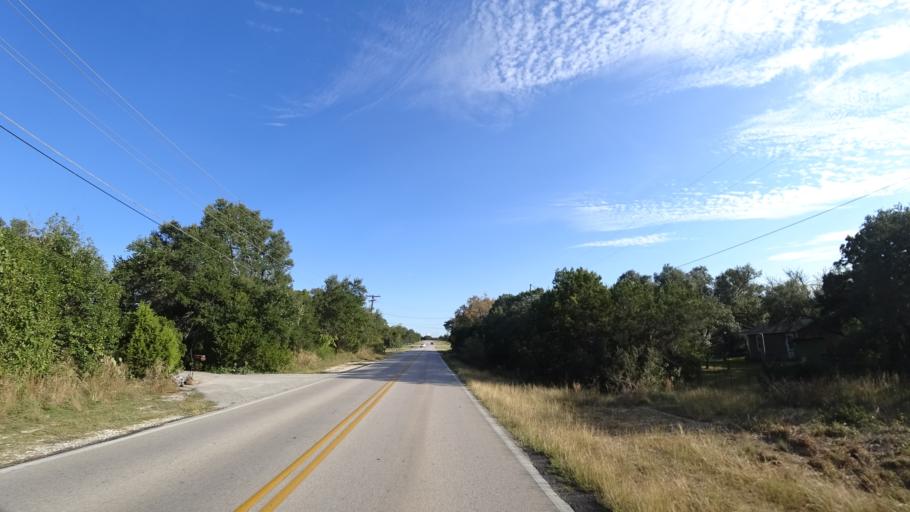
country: US
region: Texas
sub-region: Travis County
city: Barton Creek
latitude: 30.2407
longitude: -97.9205
